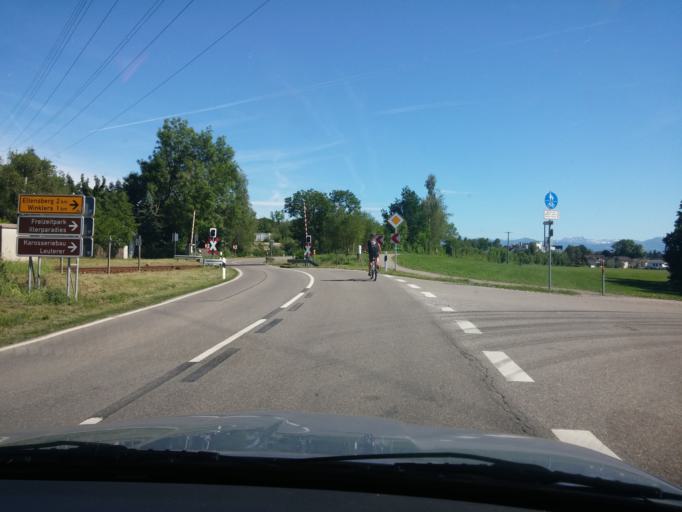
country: DE
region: Bavaria
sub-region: Swabia
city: Lauben
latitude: 47.7889
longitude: 10.3158
